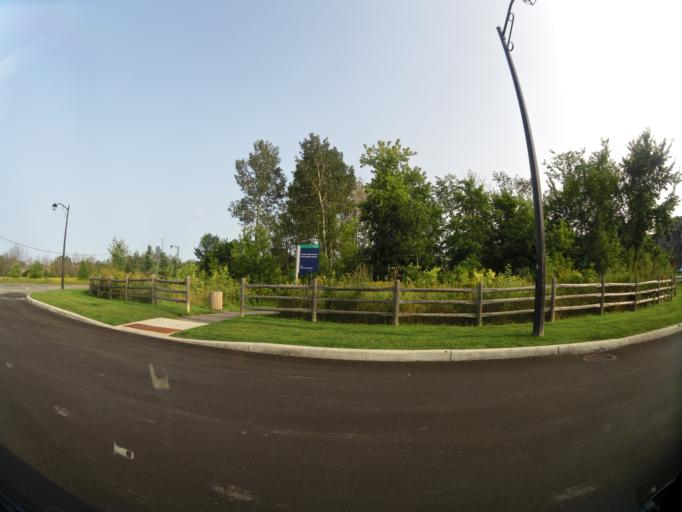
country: CA
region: Quebec
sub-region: Outaouais
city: Gatineau
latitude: 45.4914
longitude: -75.4955
